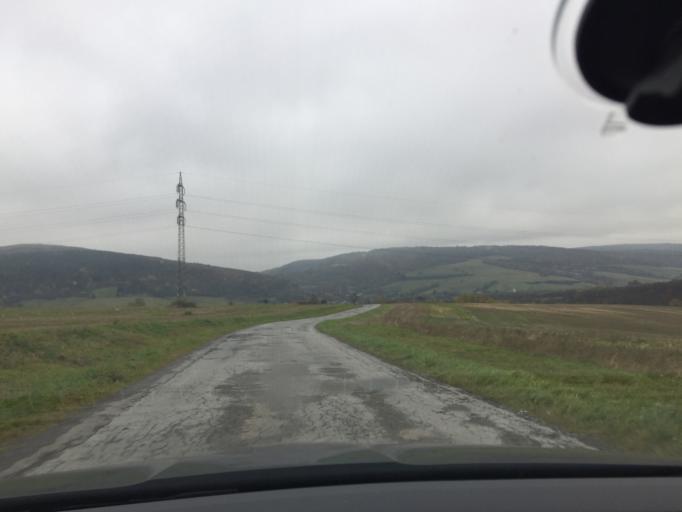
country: SK
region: Presovsky
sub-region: Okres Bardejov
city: Bardejov
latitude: 49.2508
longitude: 21.2224
